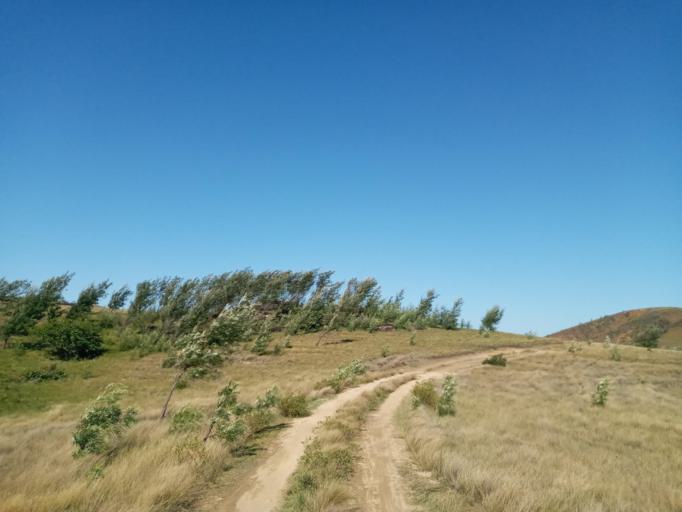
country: MG
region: Anosy
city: Fort Dauphin
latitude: -24.9107
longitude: 47.0703
